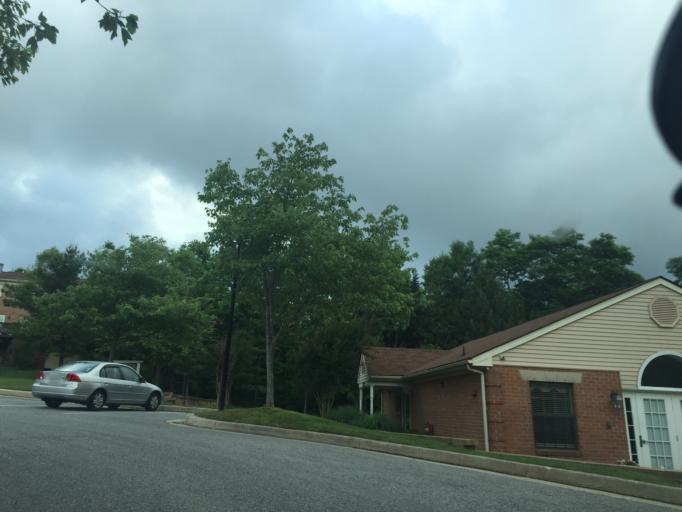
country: US
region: Maryland
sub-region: Baltimore County
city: Carney
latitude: 39.3997
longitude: -76.4933
